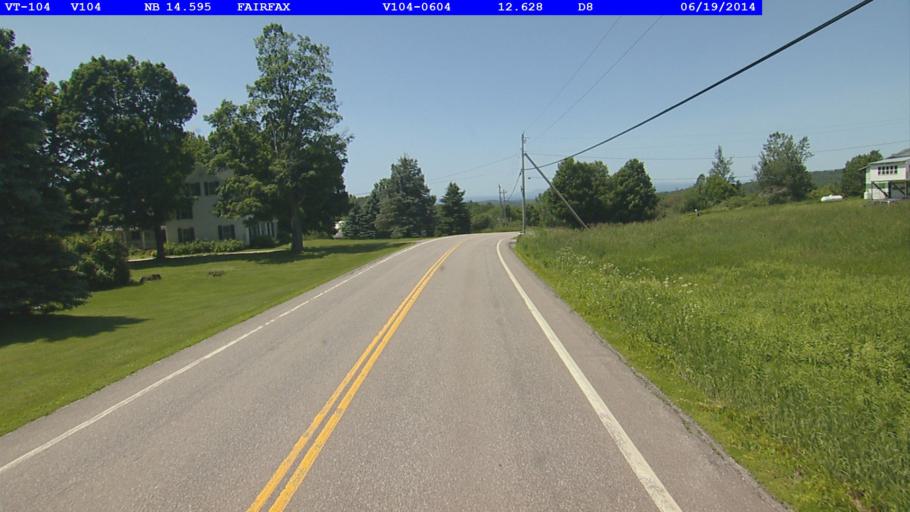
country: US
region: Vermont
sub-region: Franklin County
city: Saint Albans
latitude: 44.7601
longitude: -73.0659
